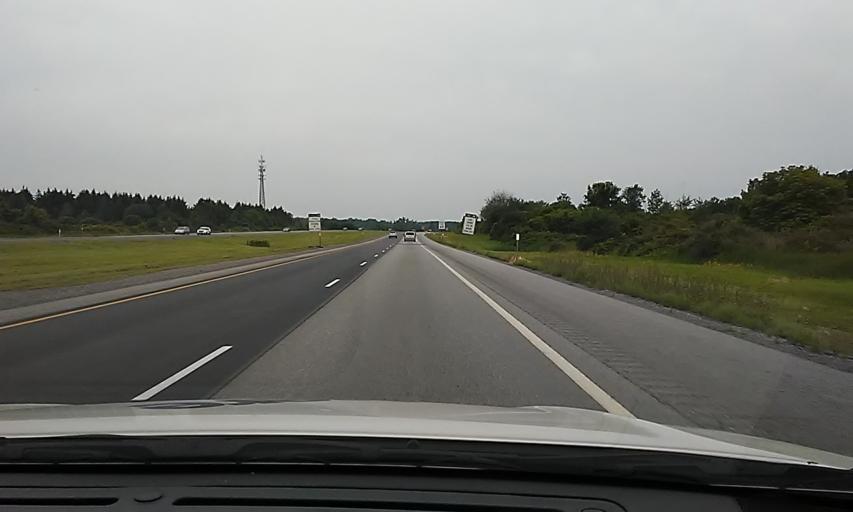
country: US
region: New York
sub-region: Genesee County
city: Batavia
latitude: 43.0157
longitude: -78.0906
